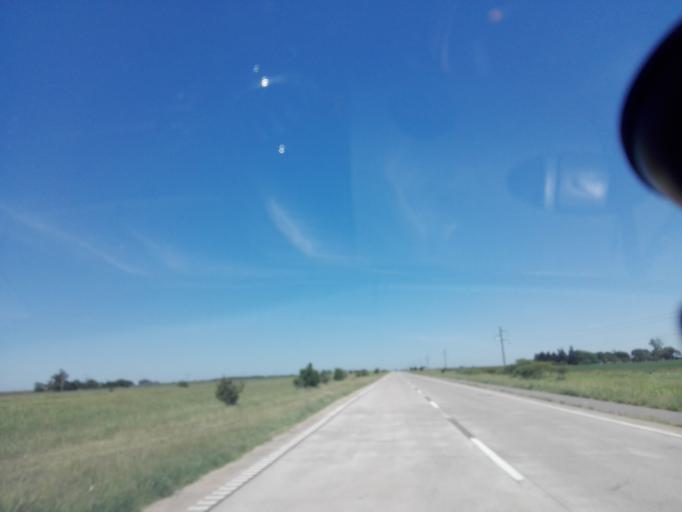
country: AR
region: Santa Fe
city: Canada de Gomez
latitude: -32.8602
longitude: -61.3105
